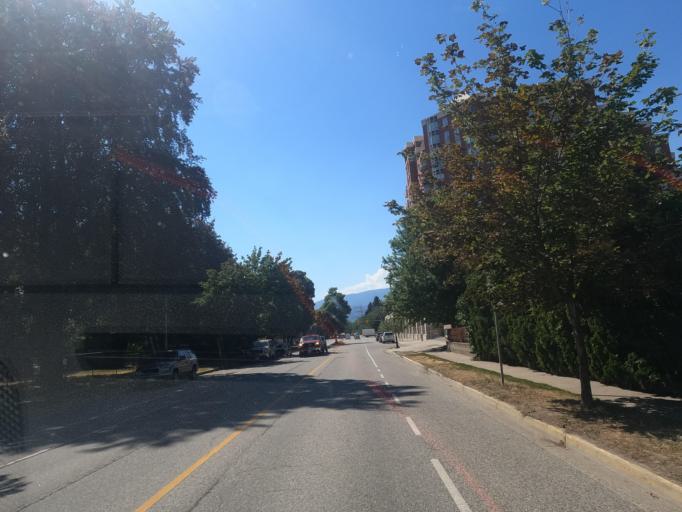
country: CA
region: British Columbia
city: Kelowna
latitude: 49.8864
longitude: -119.4744
